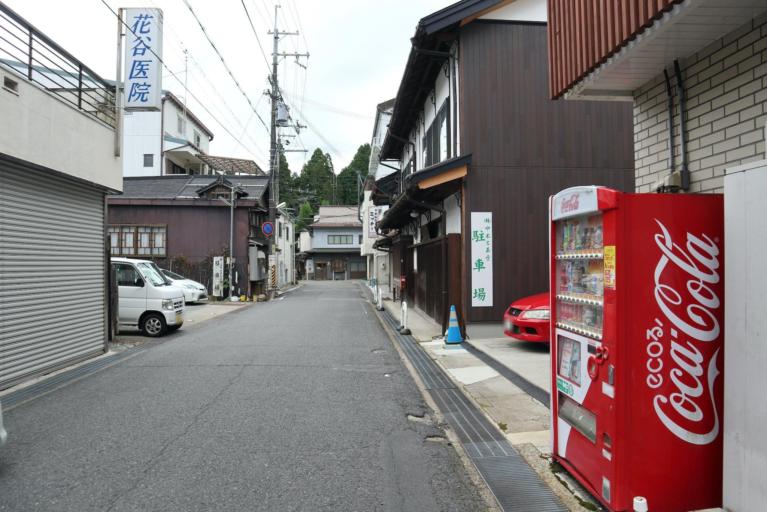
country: JP
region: Wakayama
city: Koya
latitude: 34.2124
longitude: 135.5875
